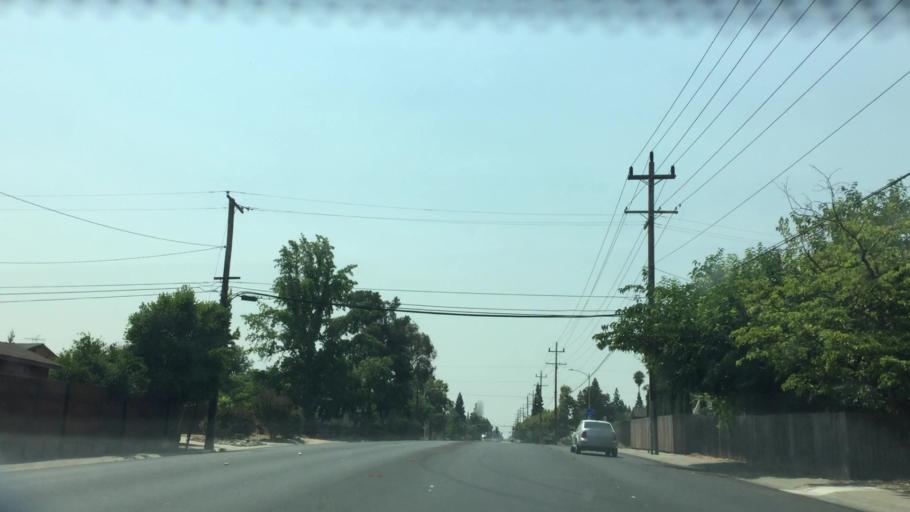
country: US
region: California
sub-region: Sacramento County
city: Arden-Arcade
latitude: 38.6242
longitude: -121.3645
